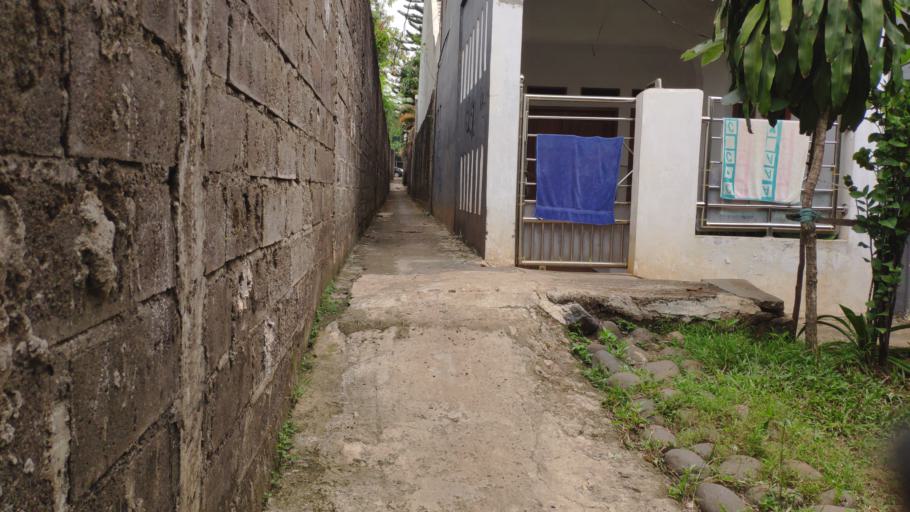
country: ID
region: West Java
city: Depok
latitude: -6.3677
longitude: 106.8069
